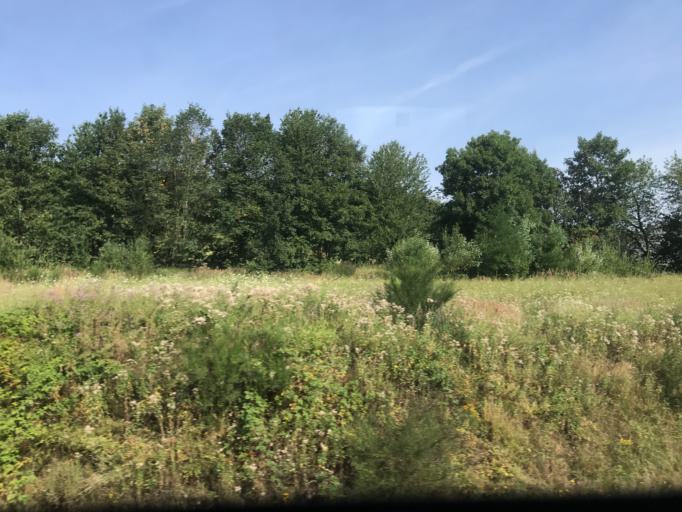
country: CZ
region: Central Bohemia
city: Votice
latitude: 49.6317
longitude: 14.6121
